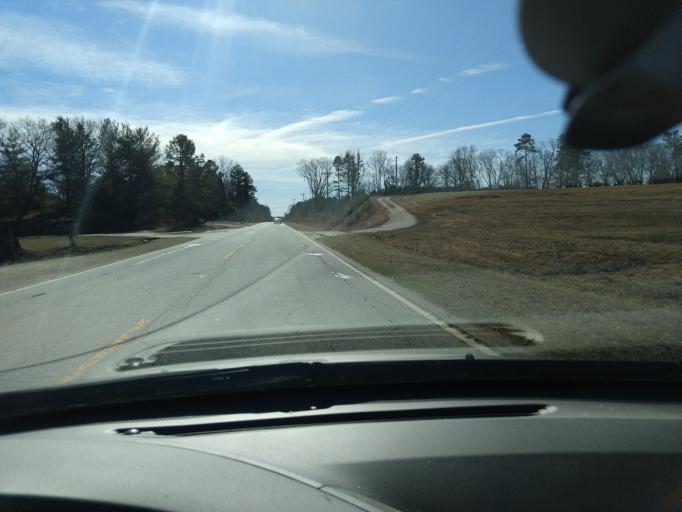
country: US
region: South Carolina
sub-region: Oconee County
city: Westminster
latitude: 34.6463
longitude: -83.1339
